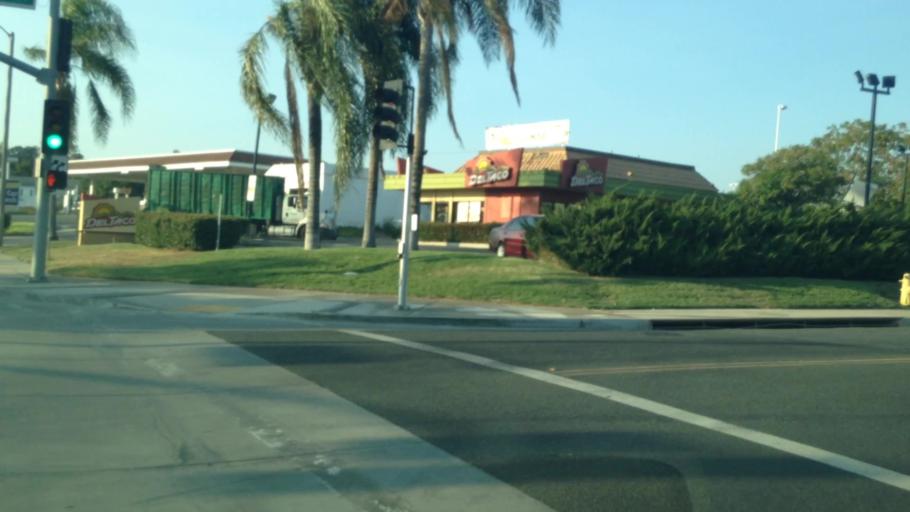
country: US
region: California
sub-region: Riverside County
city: Pedley
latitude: 33.9760
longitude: -117.4622
